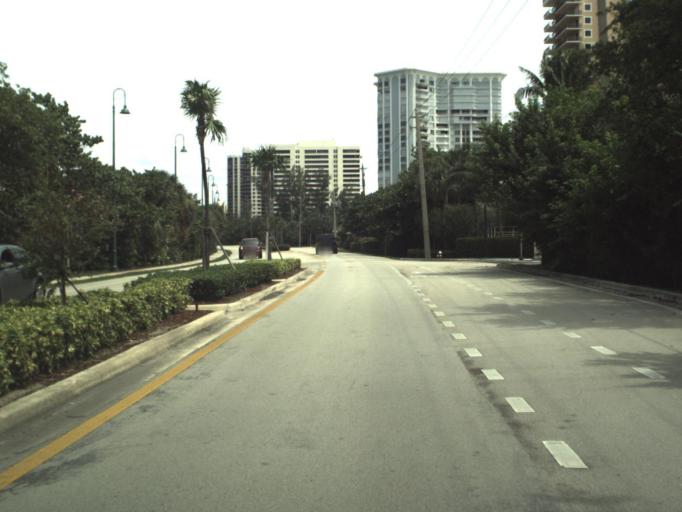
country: US
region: Florida
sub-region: Palm Beach County
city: Palm Beach Shores
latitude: 26.8009
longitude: -80.0341
